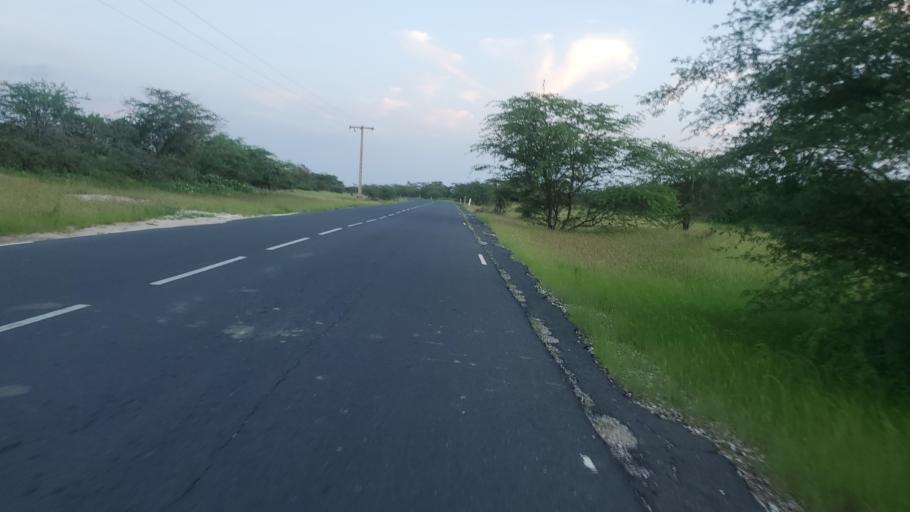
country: SN
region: Saint-Louis
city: Saint-Louis
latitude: 16.1045
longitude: -16.4116
